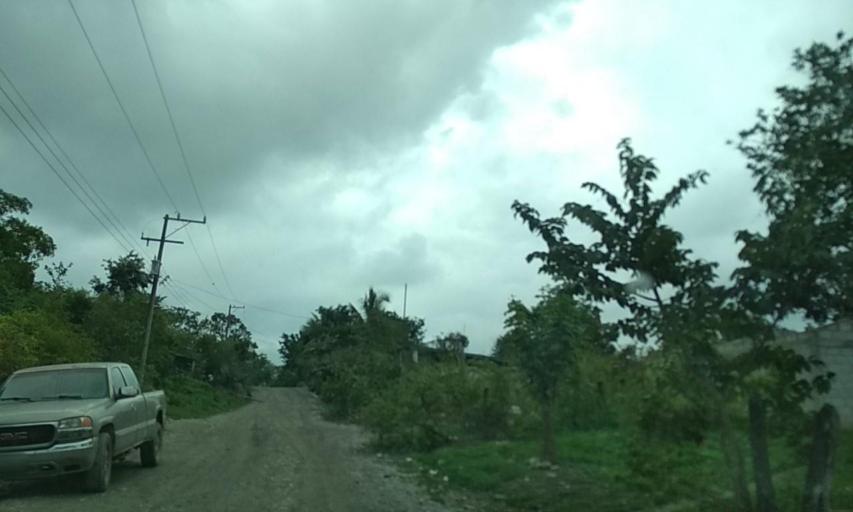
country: MX
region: Puebla
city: Espinal
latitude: 20.3187
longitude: -97.4163
